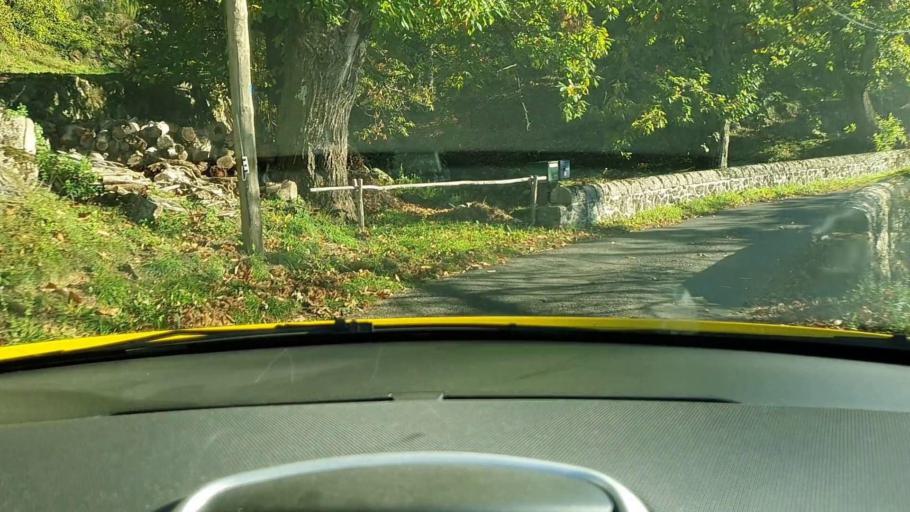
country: FR
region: Languedoc-Roussillon
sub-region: Departement du Gard
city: Sumene
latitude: 44.0181
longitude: 3.7772
